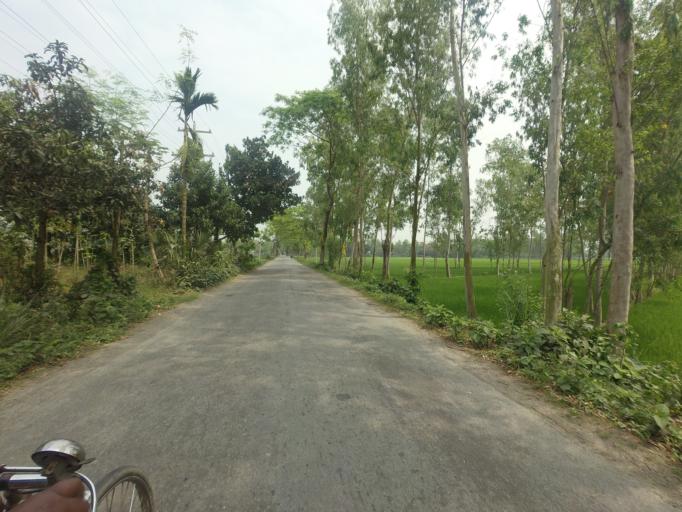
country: BD
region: Rajshahi
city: Sirajganj
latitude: 24.3876
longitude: 89.6853
